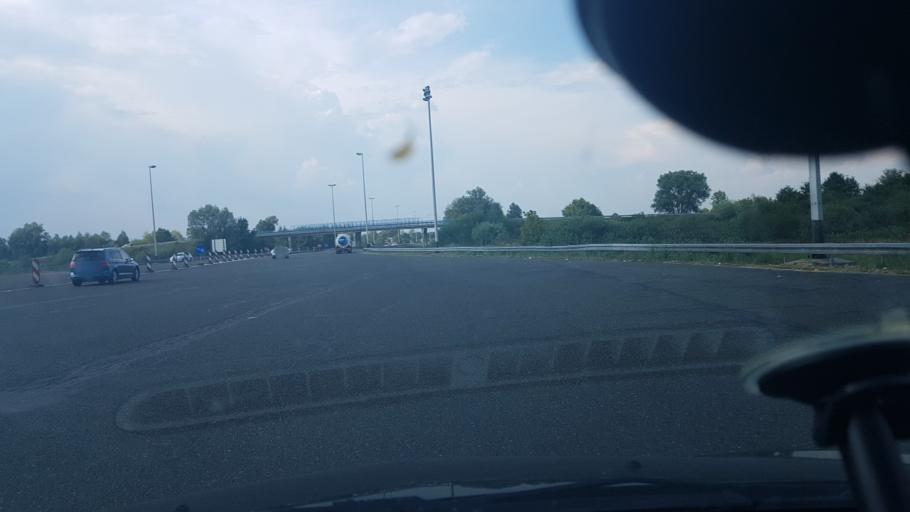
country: HR
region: Zagrebacka
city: Jablanovec
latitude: 45.8757
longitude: 15.8299
